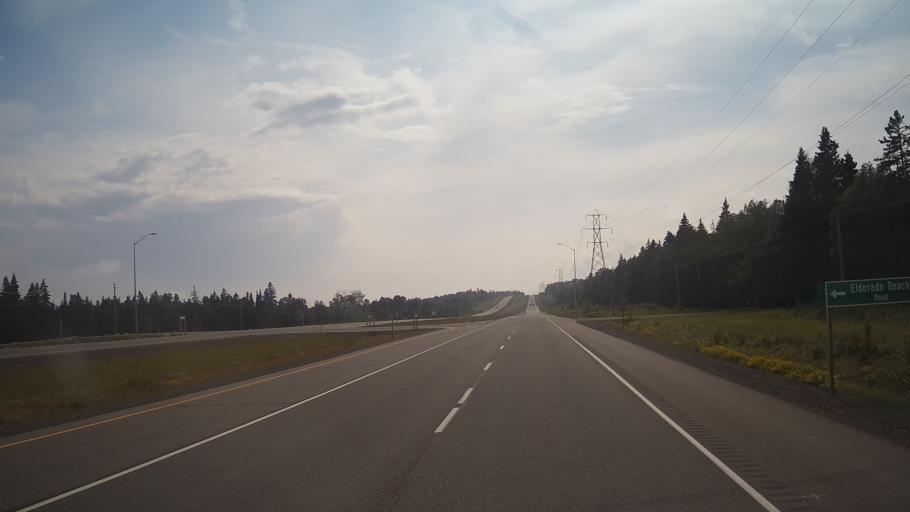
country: CA
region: Ontario
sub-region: Thunder Bay District
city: Thunder Bay
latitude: 48.5786
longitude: -88.8115
